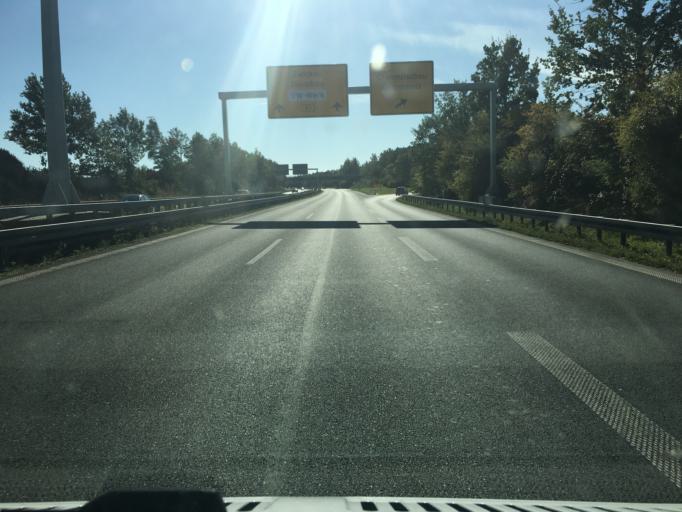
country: DE
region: Saxony
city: Dennheritz
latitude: 50.8193
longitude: 12.4495
